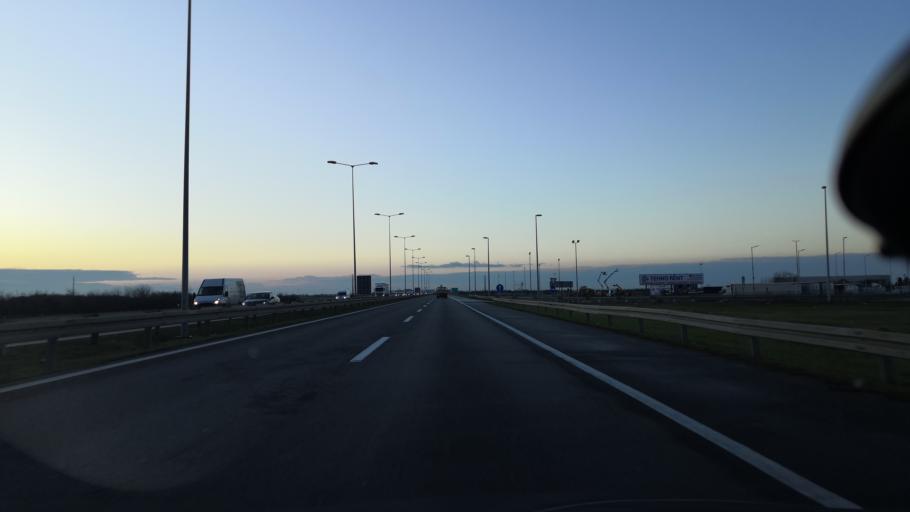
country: RS
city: Dobanovci
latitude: 44.8452
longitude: 20.2081
